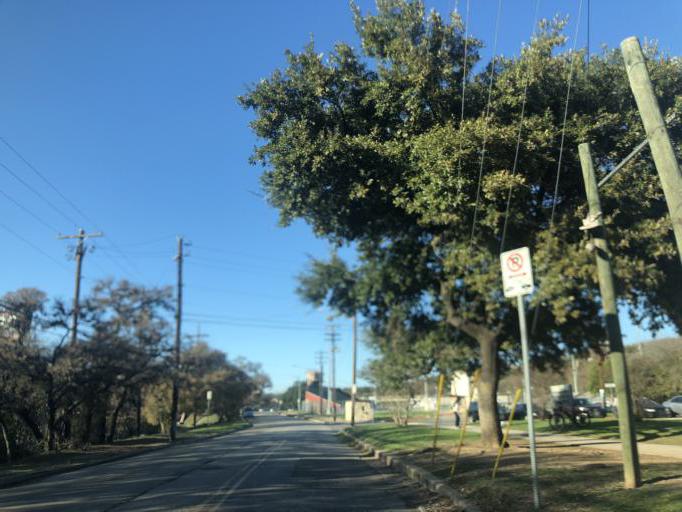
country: US
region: Texas
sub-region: Travis County
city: Austin
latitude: 30.2770
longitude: -97.7500
